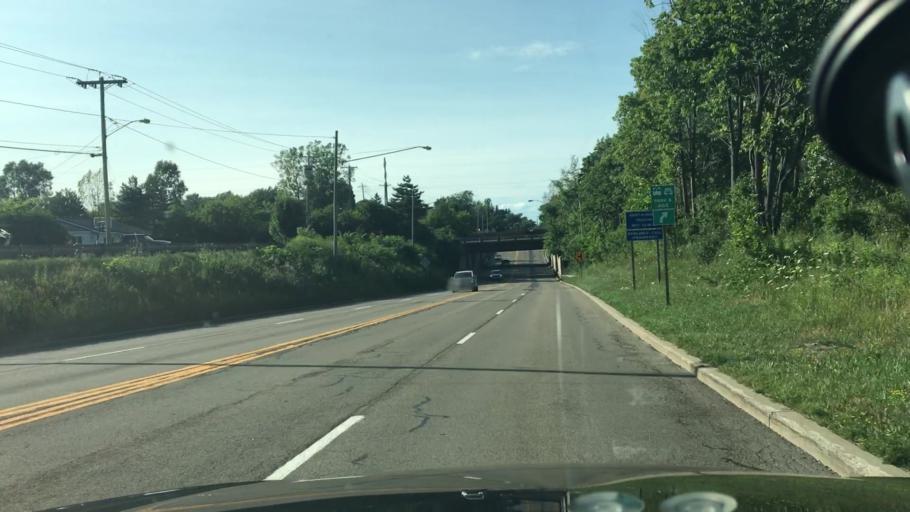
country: US
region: New York
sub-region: Erie County
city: Wanakah
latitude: 42.7634
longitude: -78.8635
